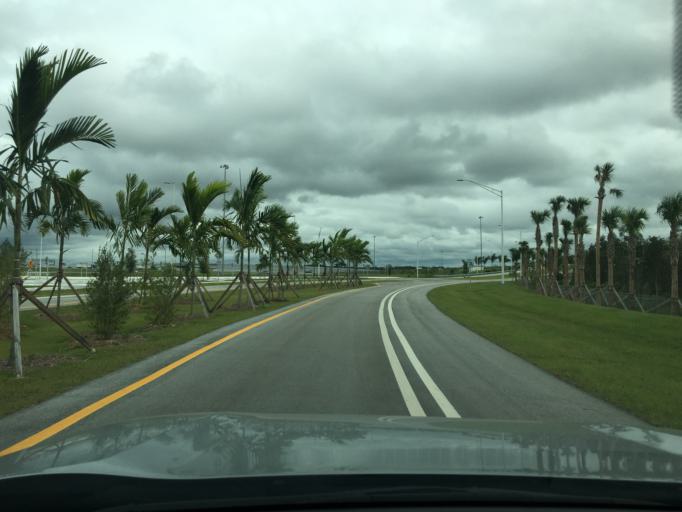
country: US
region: Florida
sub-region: Miami-Dade County
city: Palm Springs North
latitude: 25.9425
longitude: -80.3563
